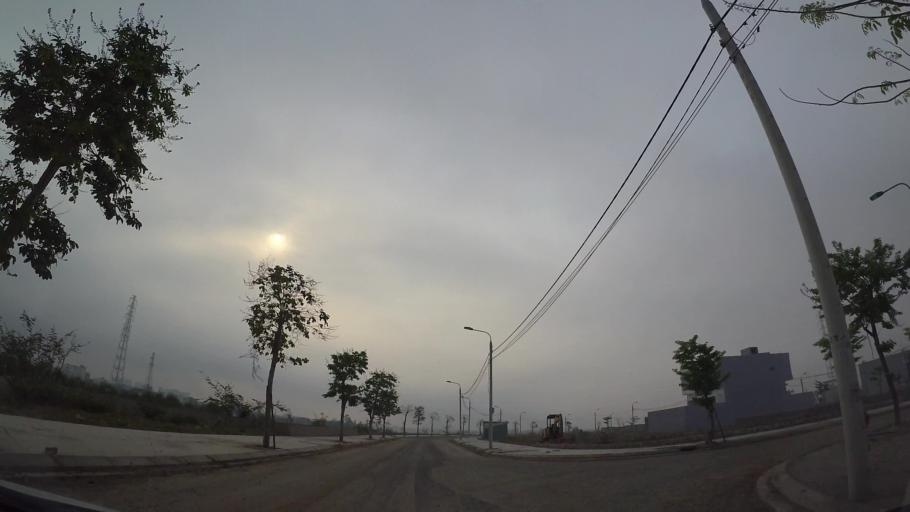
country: VN
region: Da Nang
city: Ngu Hanh Son
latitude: 16.0233
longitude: 108.2369
